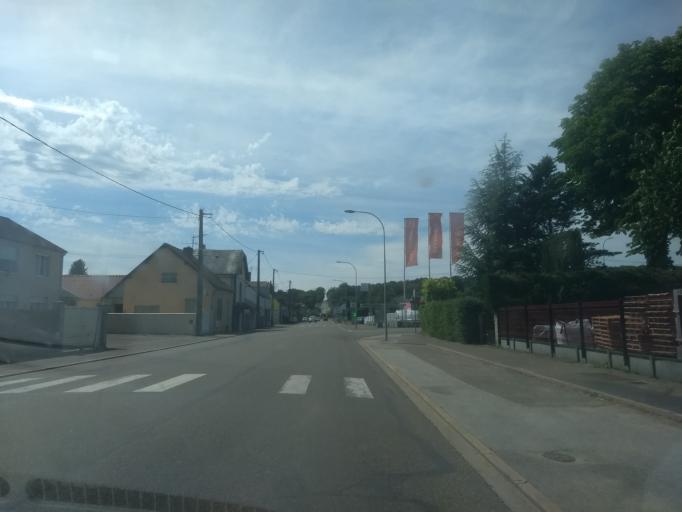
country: FR
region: Centre
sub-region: Departement d'Eure-et-Loir
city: Nogent-le-Rotrou
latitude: 48.3274
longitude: 0.8043
